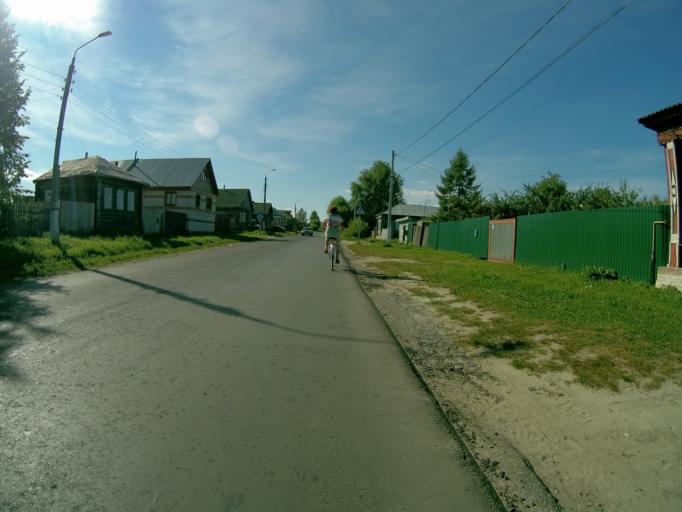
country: RU
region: Vladimir
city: Sudogda
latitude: 55.9525
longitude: 40.8469
